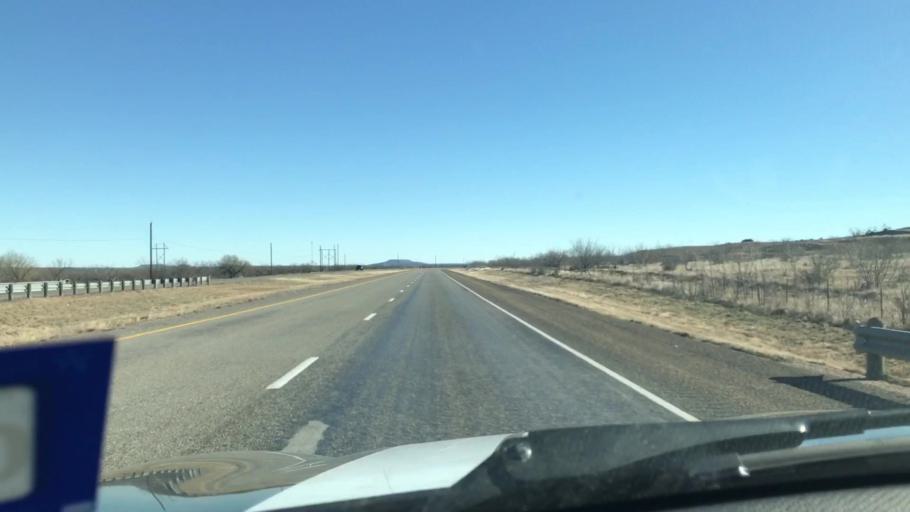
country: US
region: Texas
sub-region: Garza County
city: Post
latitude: 33.0634
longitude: -101.2215
